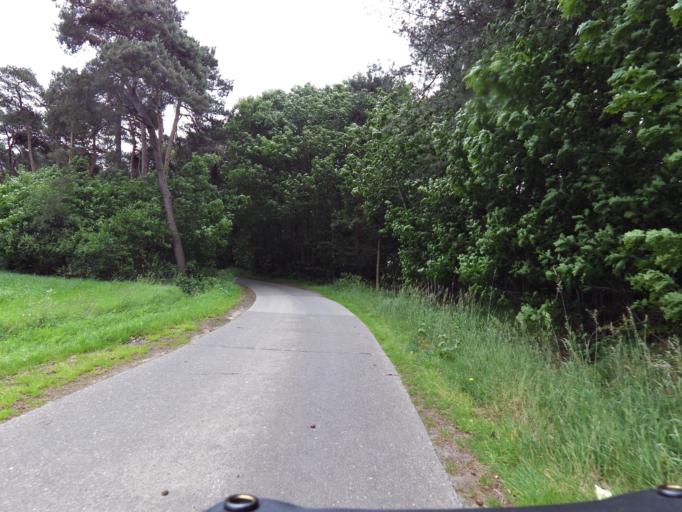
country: BE
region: Flanders
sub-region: Provincie Antwerpen
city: Baarle-Hertog
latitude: 51.4717
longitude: 4.8351
